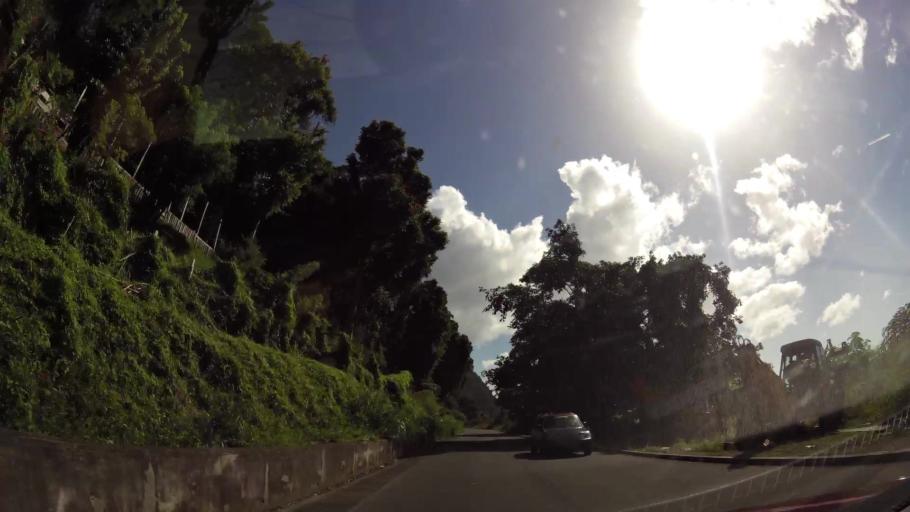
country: DM
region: Saint Luke
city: Pointe Michel
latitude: 15.2818
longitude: -61.3746
